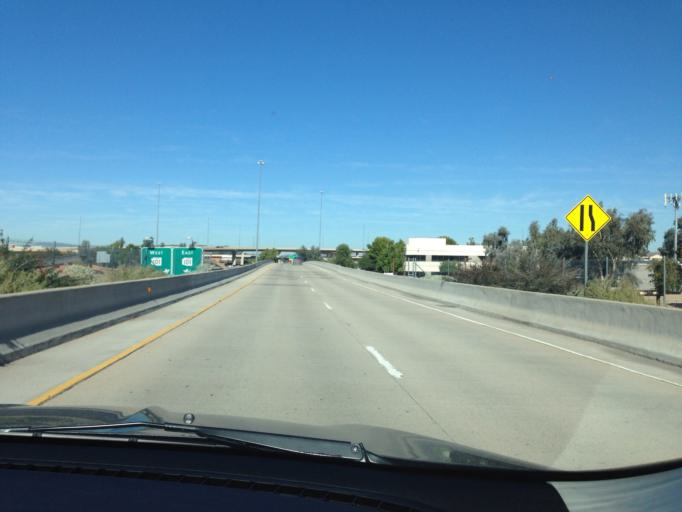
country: US
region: Arizona
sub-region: Maricopa County
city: Glendale
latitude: 33.6629
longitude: -112.1133
